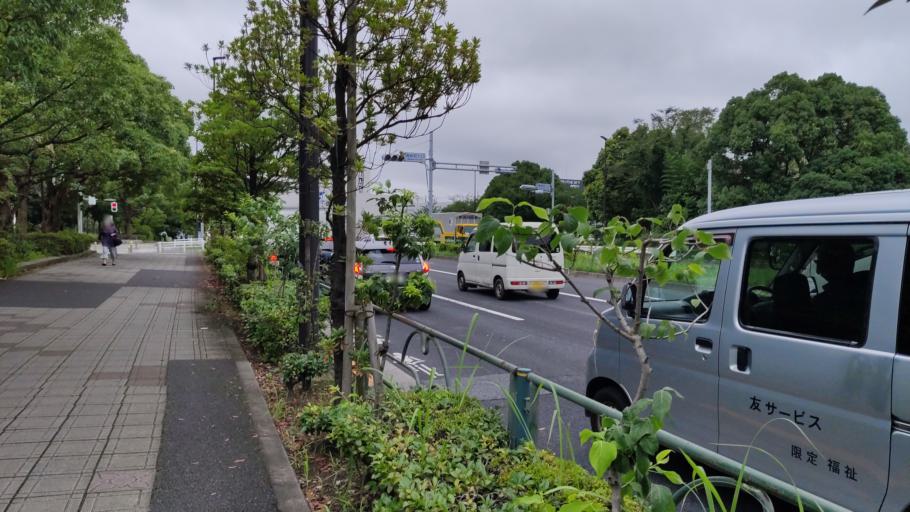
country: JP
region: Tokyo
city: Urayasu
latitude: 35.6632
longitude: 139.8561
